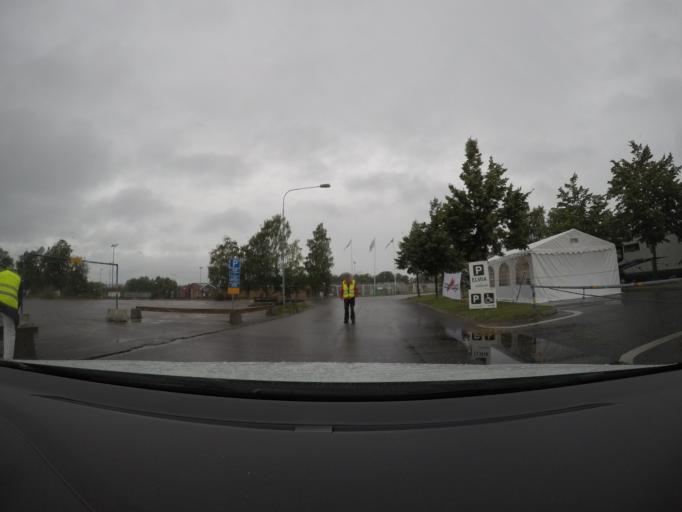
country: SE
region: Joenkoeping
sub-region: Jonkopings Kommun
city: Jonkoping
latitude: 57.7886
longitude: 14.2248
